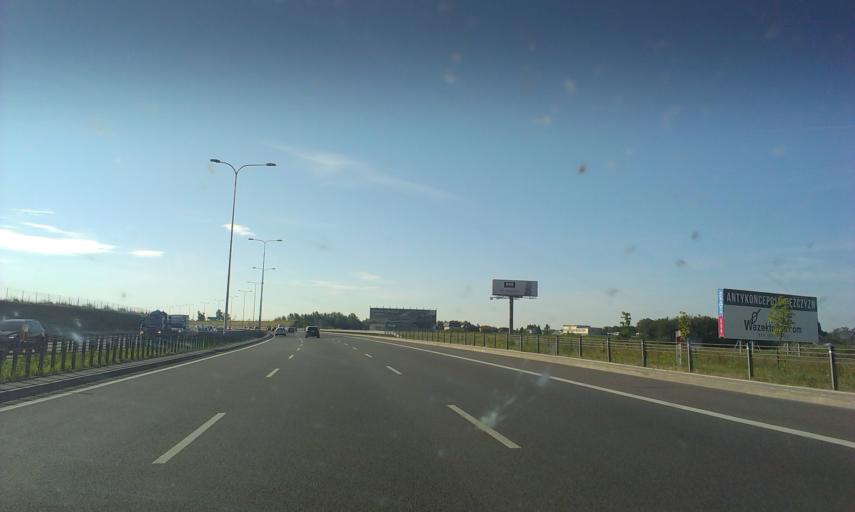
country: PL
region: Masovian Voivodeship
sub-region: Powiat pruszkowski
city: Rybie
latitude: 52.1433
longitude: 20.9671
